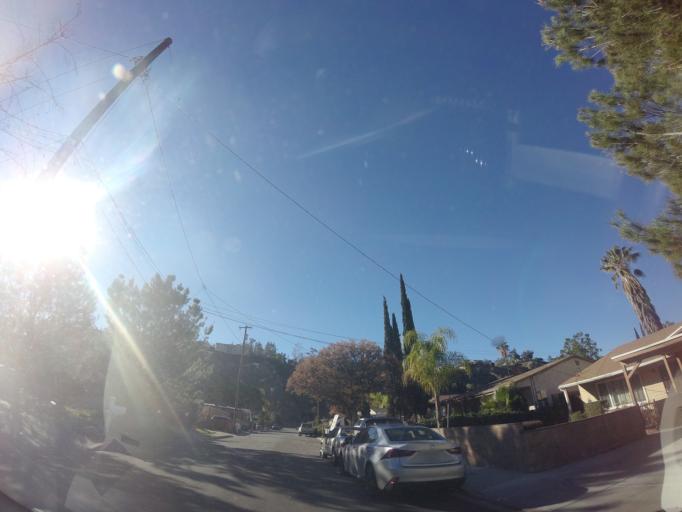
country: US
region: California
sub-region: Los Angeles County
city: Burbank
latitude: 34.2652
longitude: -118.3373
